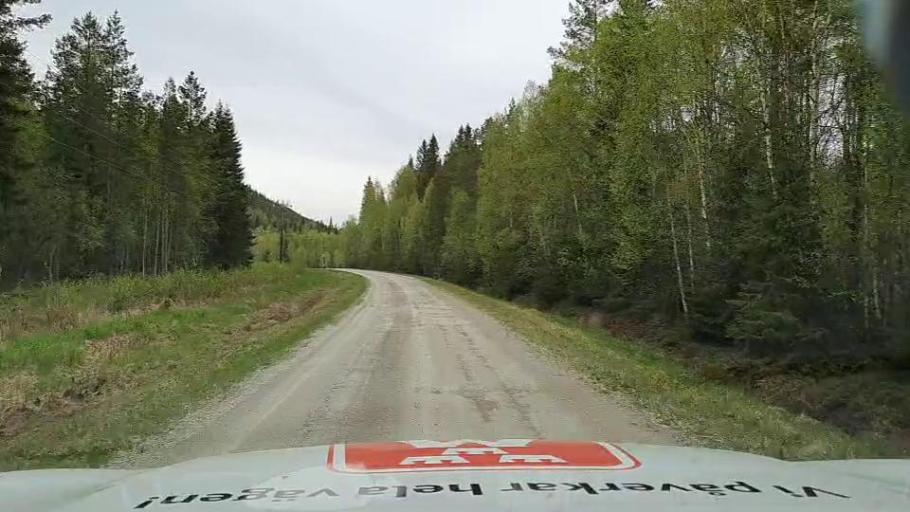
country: SE
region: Jaemtland
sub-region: Bergs Kommun
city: Hoverberg
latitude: 62.6813
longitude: 14.7980
